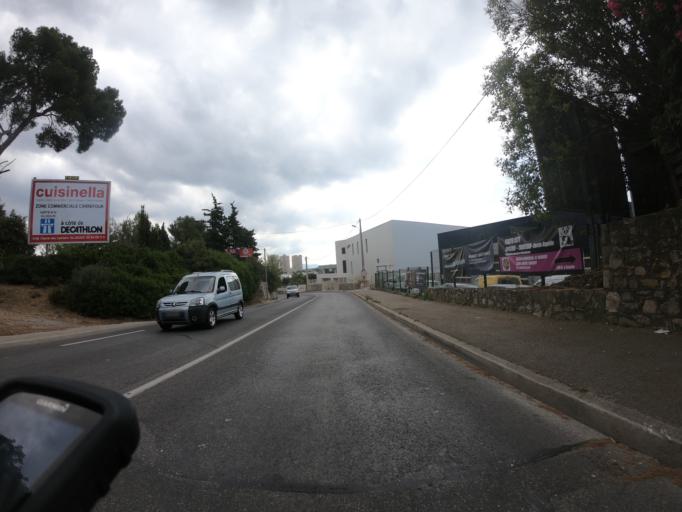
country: FR
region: Provence-Alpes-Cote d'Azur
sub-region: Departement du Var
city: Six-Fours-les-Plages
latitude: 43.1090
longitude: 5.8550
